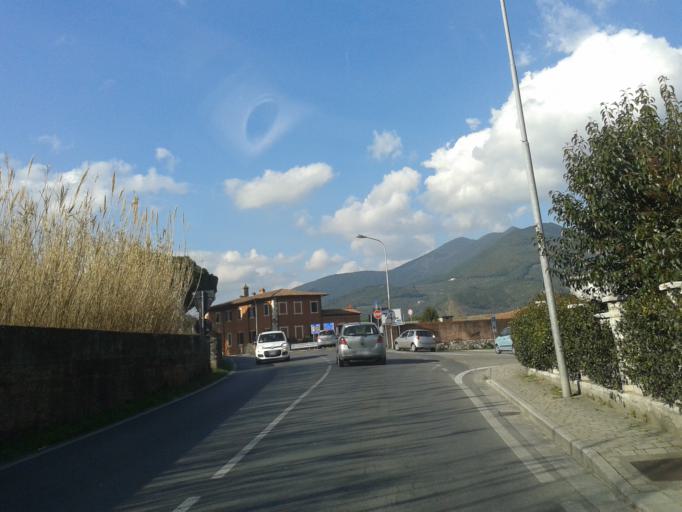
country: IT
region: Tuscany
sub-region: Province of Pisa
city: Uliveto Terme
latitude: 43.7073
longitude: 10.5041
